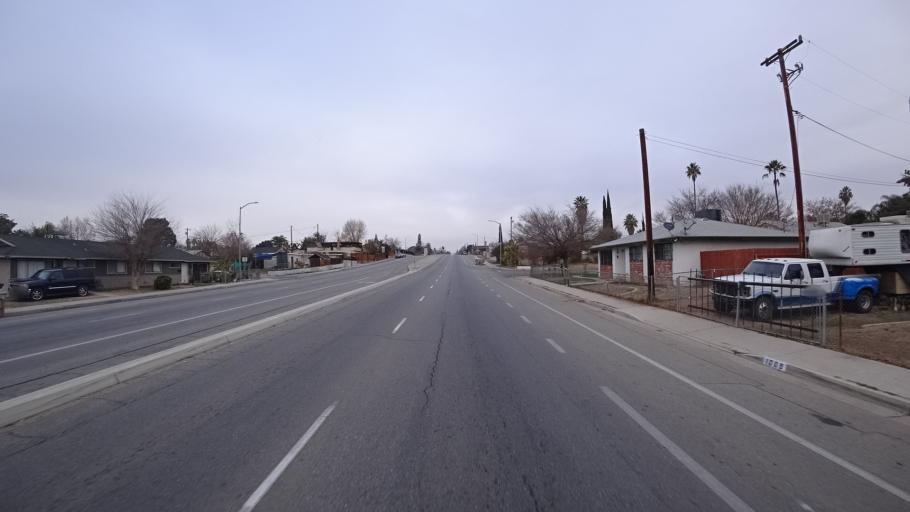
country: US
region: California
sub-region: Kern County
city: Bakersfield
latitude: 35.3726
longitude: -118.9497
